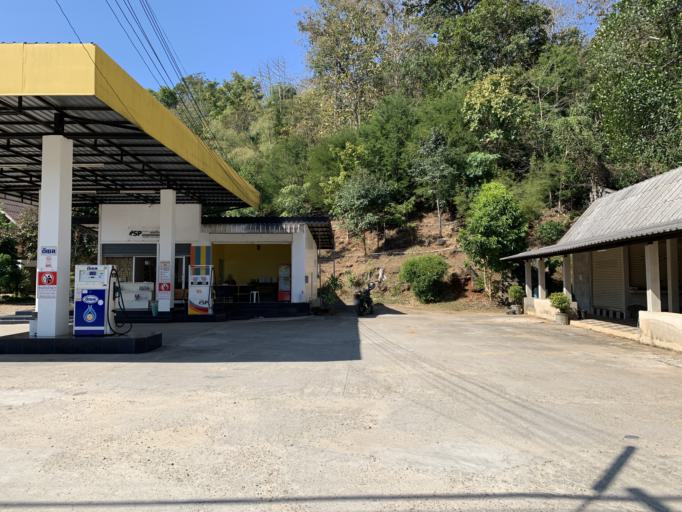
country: TH
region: Tak
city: Umphang
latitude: 16.0451
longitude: 98.8493
